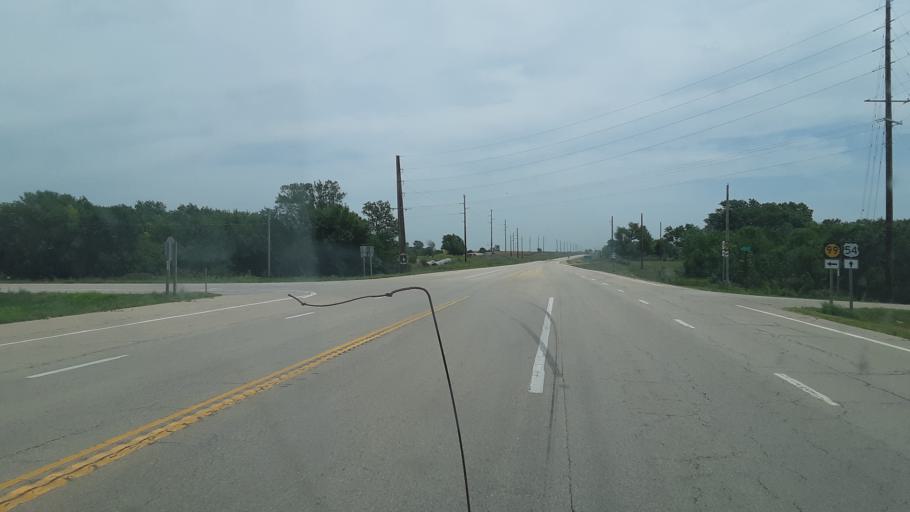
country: US
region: Kansas
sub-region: Greenwood County
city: Eureka
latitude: 37.8387
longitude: -96.1781
